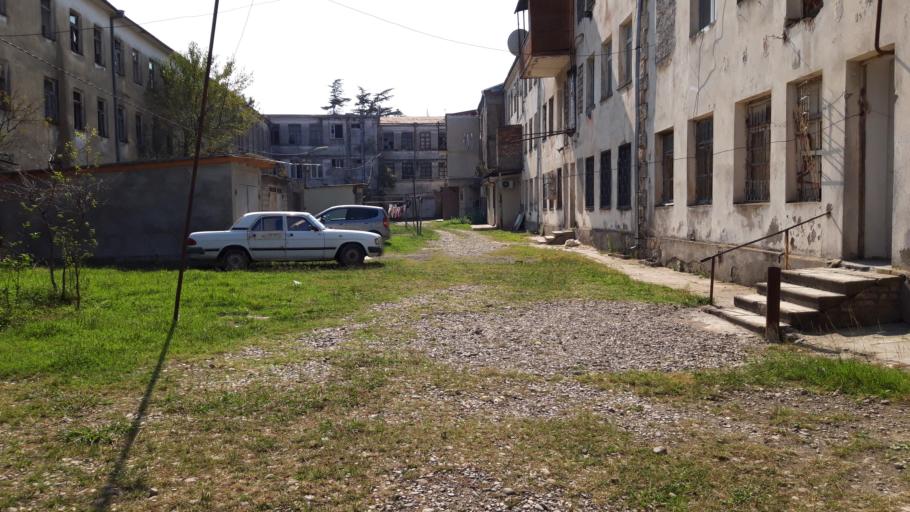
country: GE
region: Imereti
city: Samtredia
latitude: 42.1630
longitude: 42.3418
